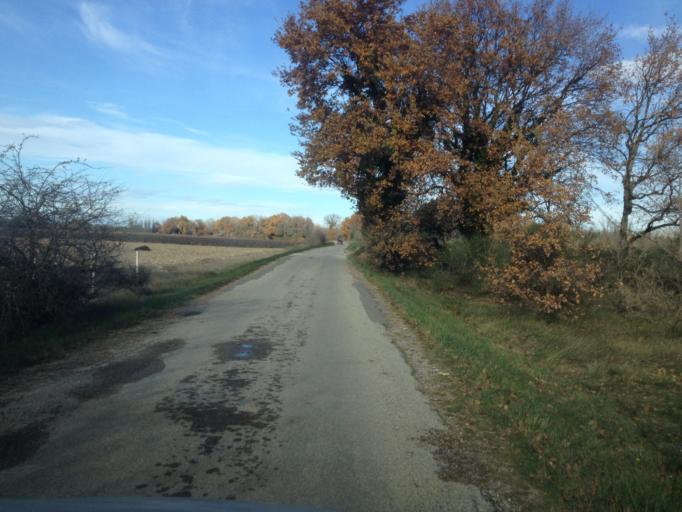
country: FR
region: Provence-Alpes-Cote d'Azur
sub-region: Departement du Vaucluse
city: Jonquieres
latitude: 44.0977
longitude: 4.9172
